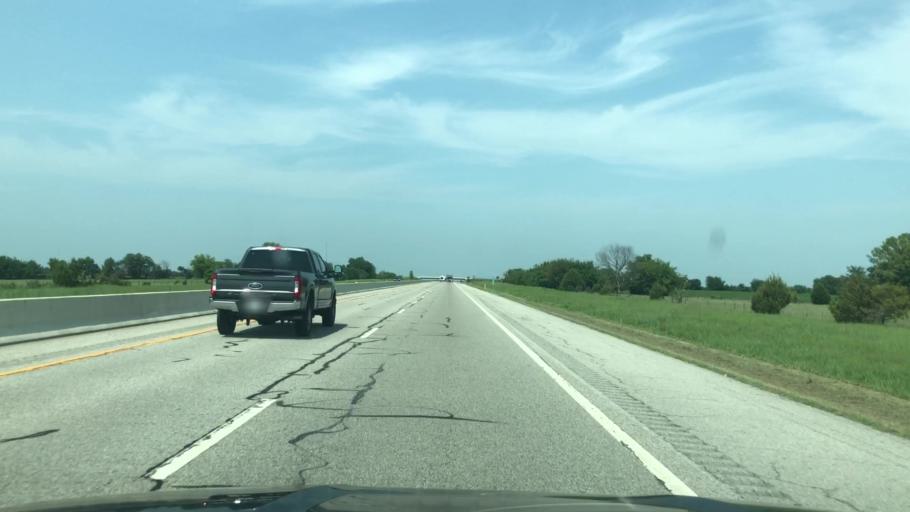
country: US
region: Oklahoma
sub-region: Ottawa County
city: Fairland
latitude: 36.7928
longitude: -94.8841
